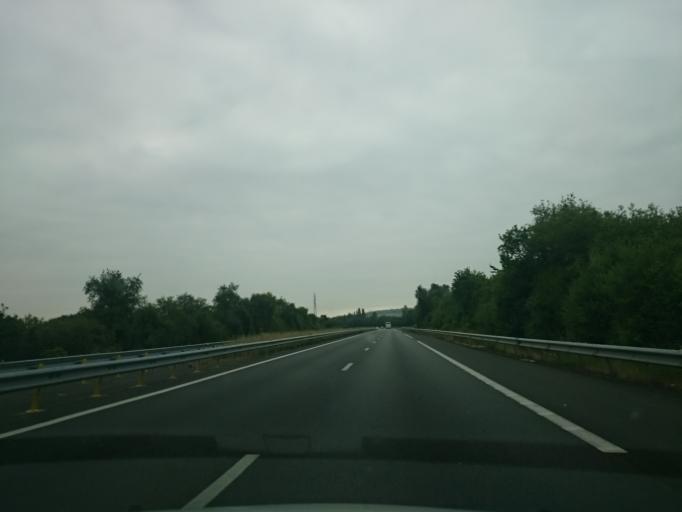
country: FR
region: Brittany
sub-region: Departement du Finistere
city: Le Faou
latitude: 48.2921
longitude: -4.1650
